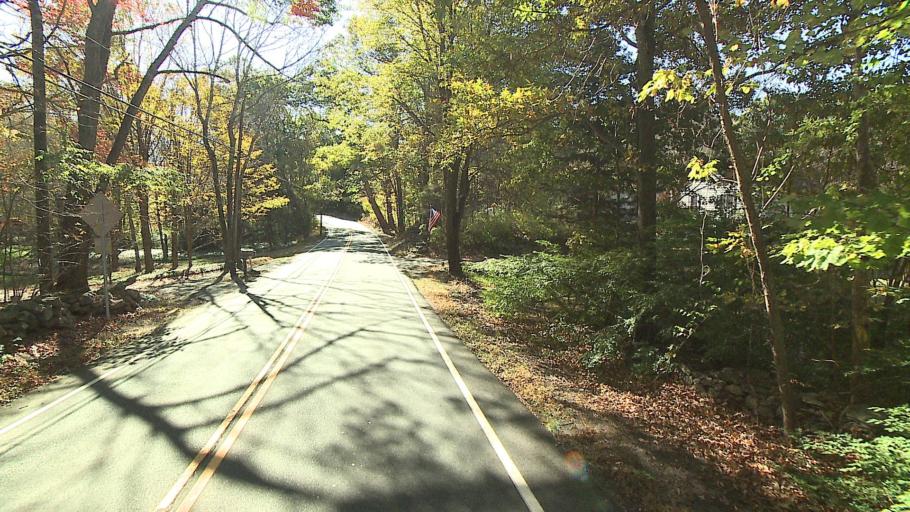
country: US
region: Connecticut
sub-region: Fairfield County
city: Trumbull
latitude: 41.2530
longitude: -73.3033
